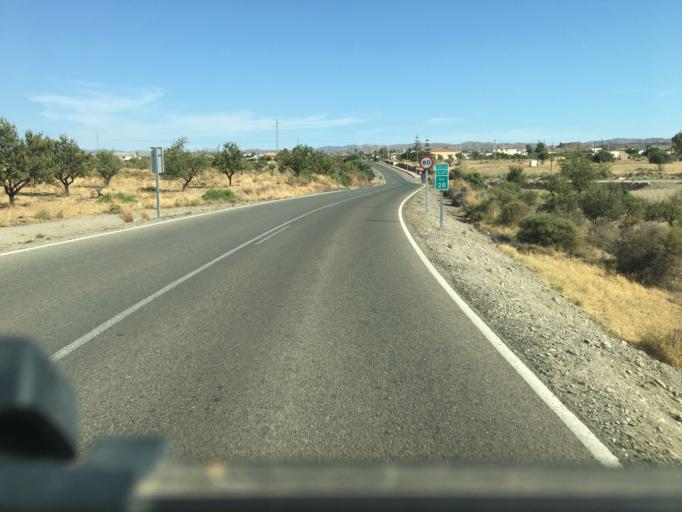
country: ES
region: Andalusia
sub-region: Provincia de Almeria
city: Huercal-Overa
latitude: 37.4439
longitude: -1.9810
